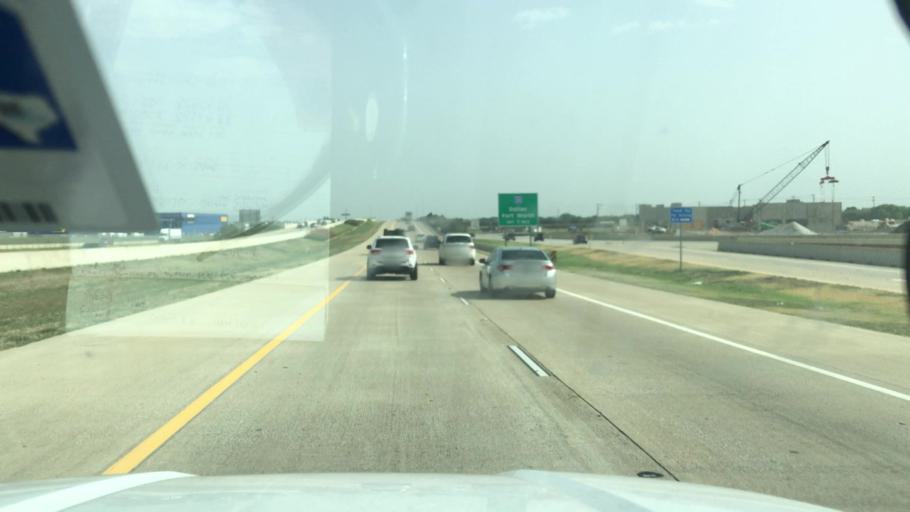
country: US
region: Texas
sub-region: Dallas County
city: Grand Prairie
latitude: 32.6956
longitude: -97.0247
